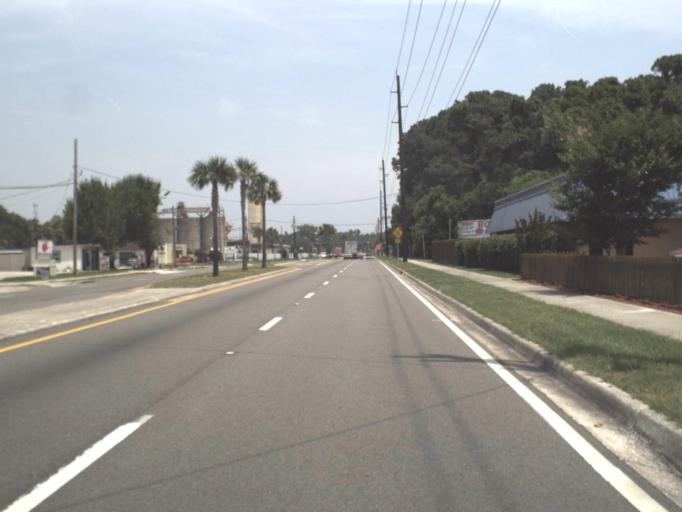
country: US
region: Florida
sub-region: Nassau County
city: Fernandina Beach
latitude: 30.6518
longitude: -81.4603
